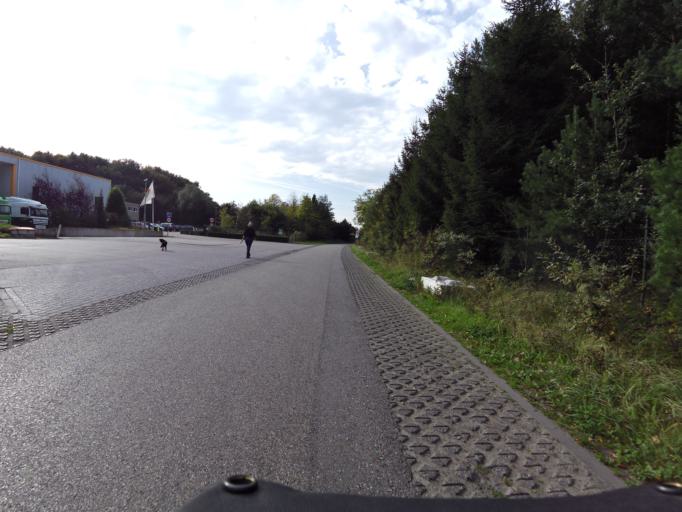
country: BE
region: Flanders
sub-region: Provincie Antwerpen
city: Stabroek
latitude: 51.3851
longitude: 4.3528
